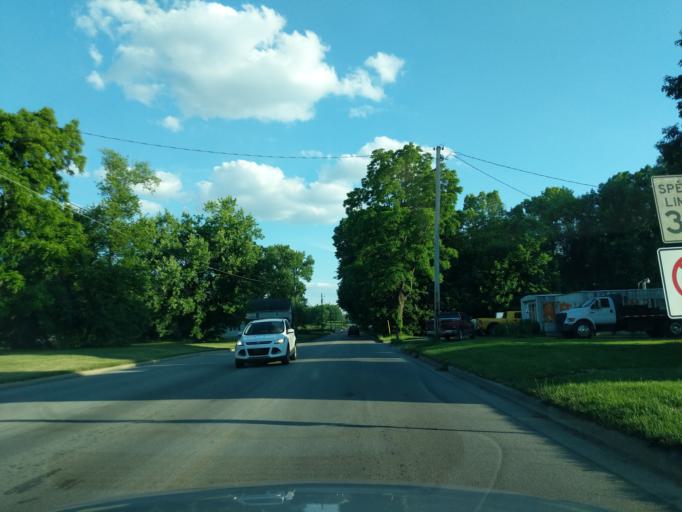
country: US
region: Indiana
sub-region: Huntington County
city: Huntington
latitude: 40.8743
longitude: -85.4710
